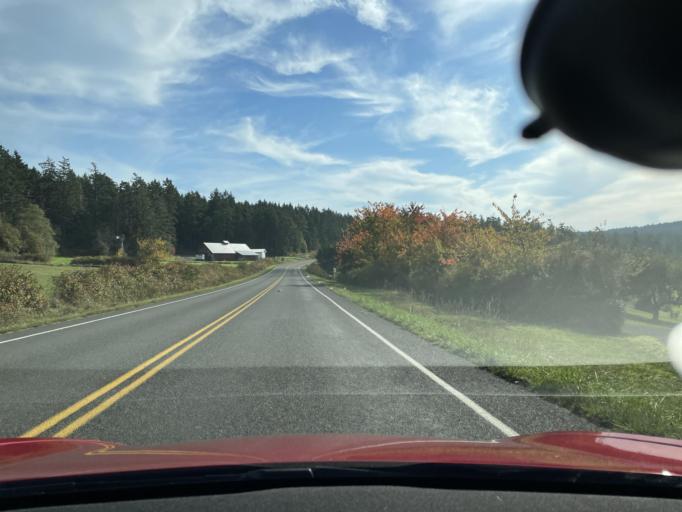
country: US
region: Washington
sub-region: San Juan County
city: Friday Harbor
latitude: 48.6091
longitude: -123.1394
